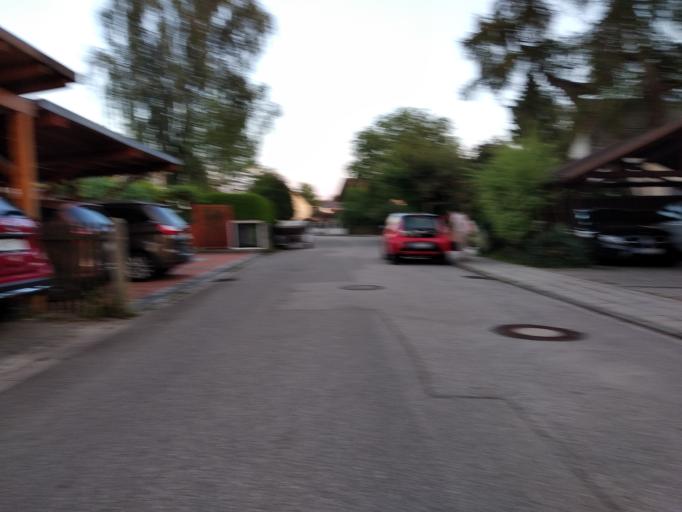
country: DE
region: Bavaria
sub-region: Upper Bavaria
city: Vaterstetten
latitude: 48.1417
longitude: 11.7849
